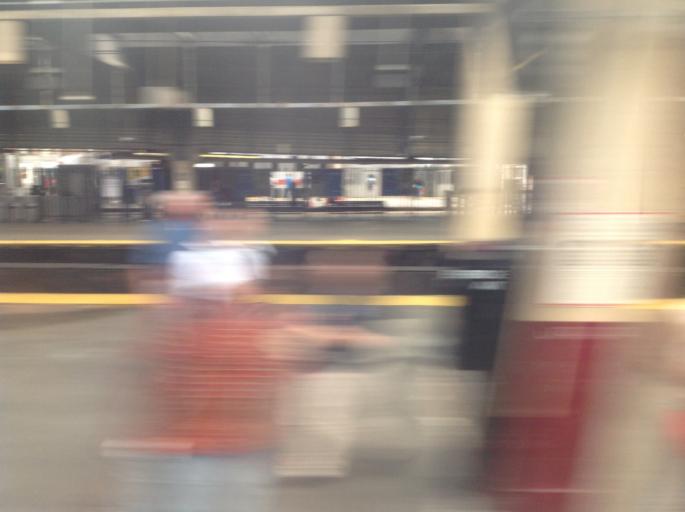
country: US
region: New Jersey
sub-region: Essex County
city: Newark
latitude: 40.7341
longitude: -74.1647
